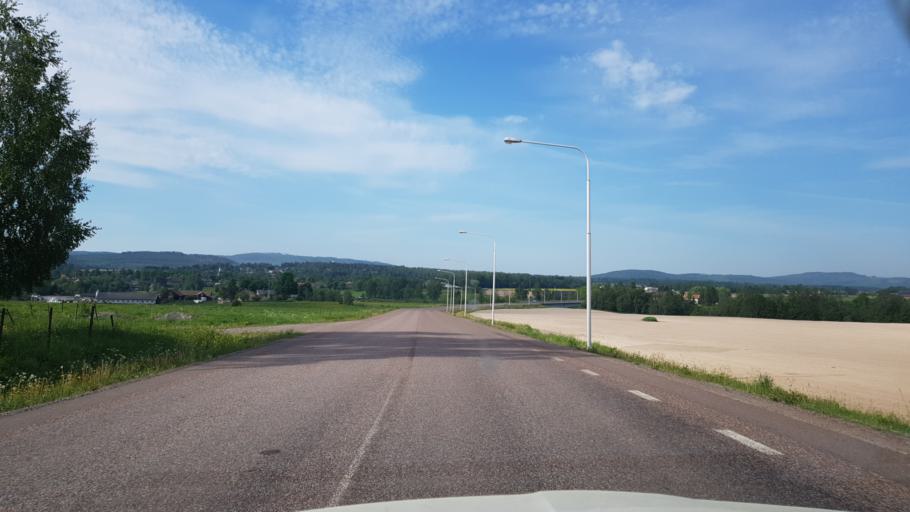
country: SE
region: Dalarna
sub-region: Borlange Kommun
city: Ornas
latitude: 60.4230
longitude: 15.6157
